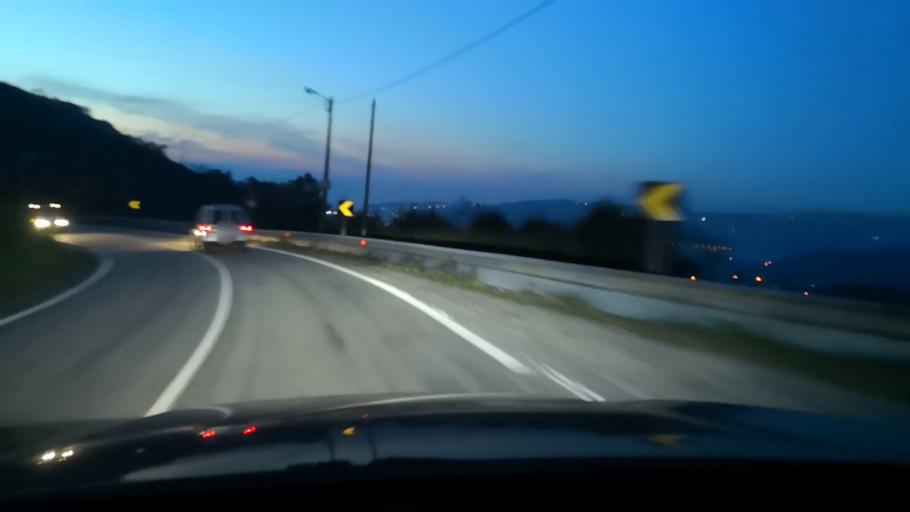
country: PT
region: Porto
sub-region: Baiao
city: Baiao
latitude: 41.2339
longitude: -8.0159
